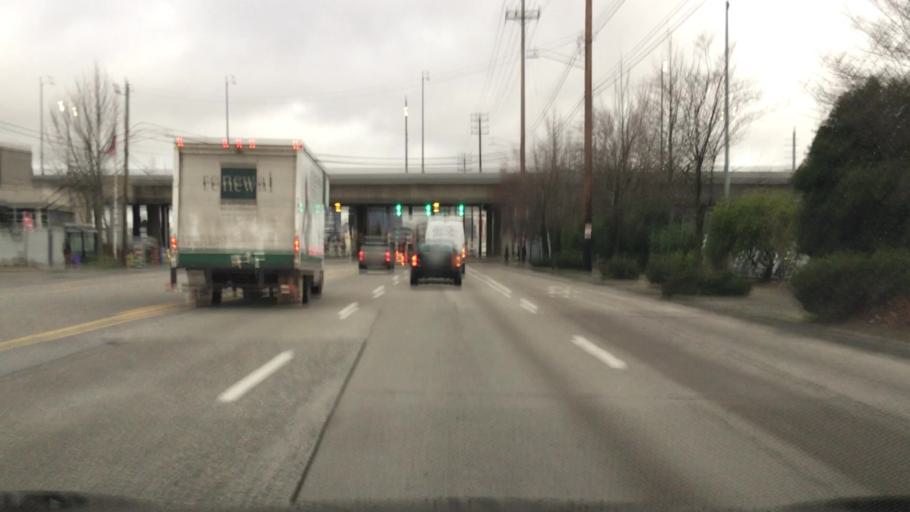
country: US
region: Washington
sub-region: King County
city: Seattle
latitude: 47.5705
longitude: -122.3290
